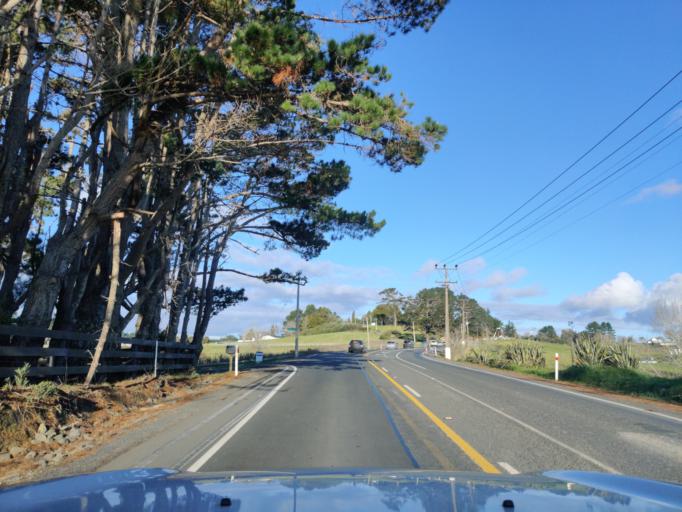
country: NZ
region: Auckland
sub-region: Auckland
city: Red Hill
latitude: -36.9660
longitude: 174.9828
